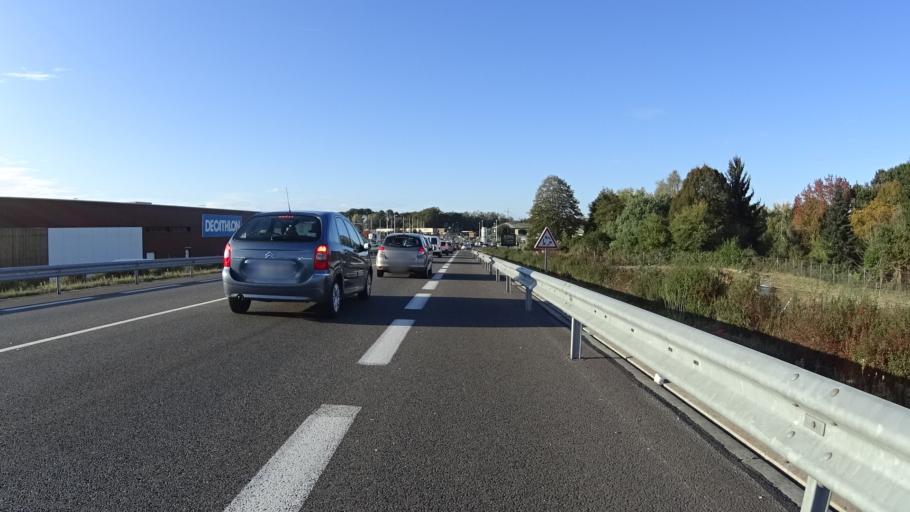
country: FR
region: Aquitaine
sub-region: Departement des Landes
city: Saint-Paul-les-Dax
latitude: 43.7285
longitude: -1.0369
